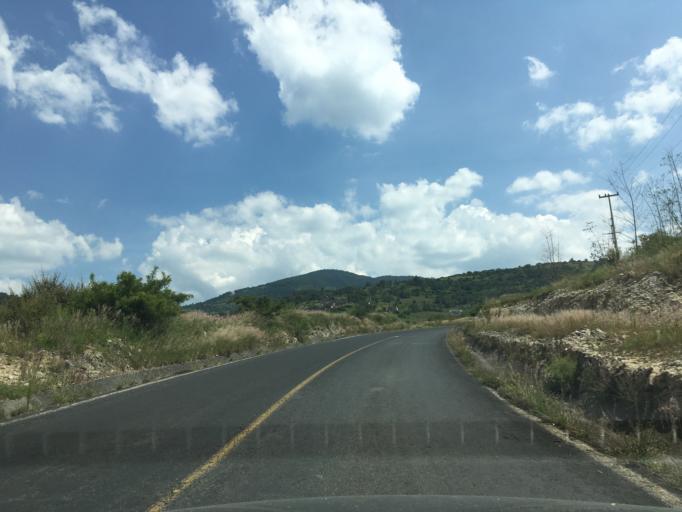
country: MX
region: Michoacan
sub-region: Morelia
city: Montana Monarca (Punta Altozano)
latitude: 19.6493
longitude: -101.2013
